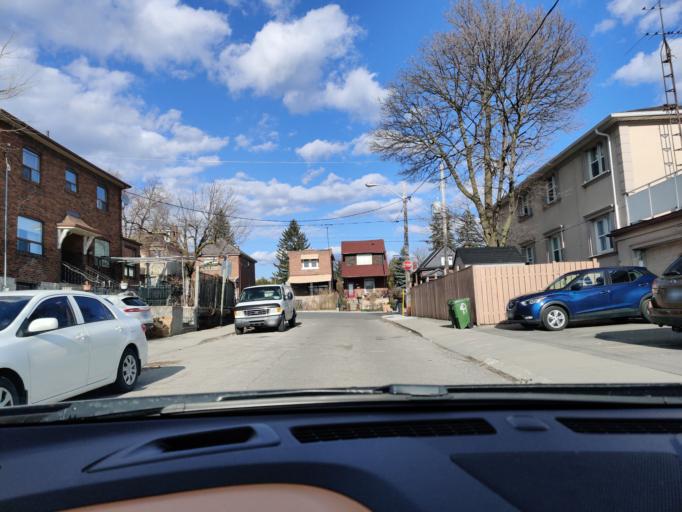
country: CA
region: Ontario
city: Toronto
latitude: 43.6885
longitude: -79.4431
